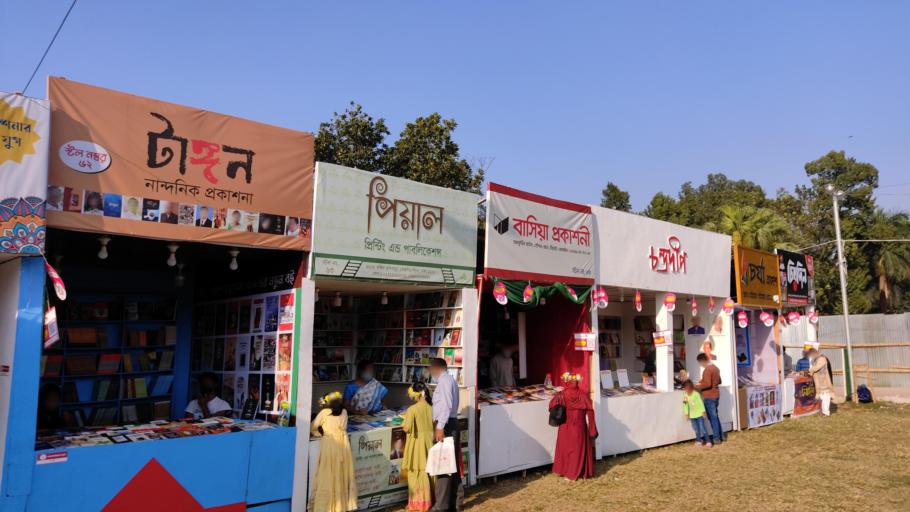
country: BD
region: Dhaka
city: Azimpur
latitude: 23.7334
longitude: 90.3995
